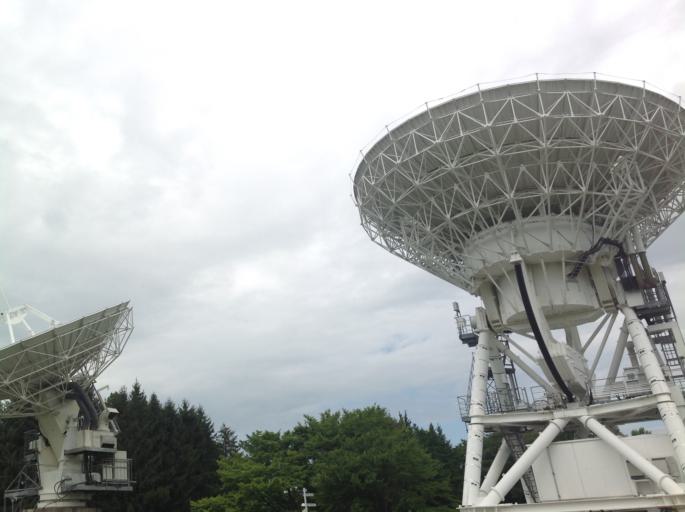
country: JP
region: Iwate
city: Mizusawa
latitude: 39.1331
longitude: 141.1326
